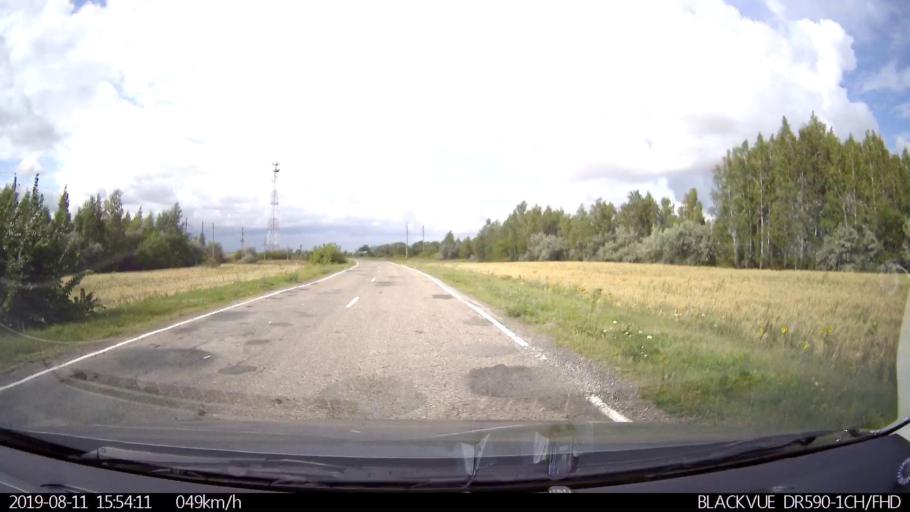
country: RU
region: Ulyanovsk
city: Ignatovka
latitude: 53.9396
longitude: 47.6567
